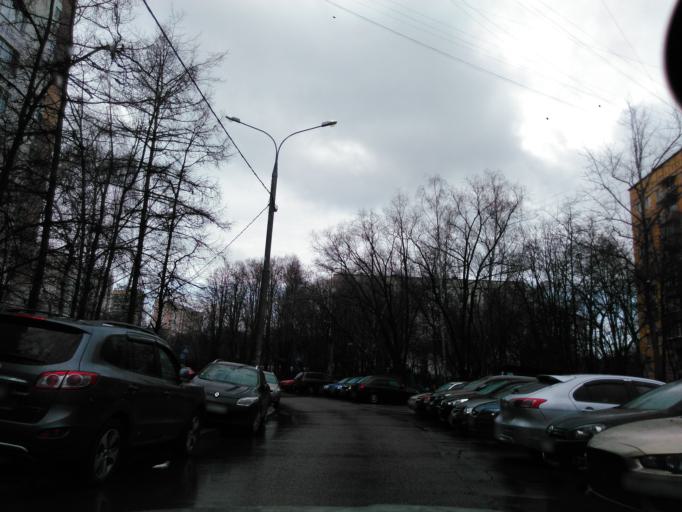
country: RU
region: Moskovskaya
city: Levoberezhnaya
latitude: 55.8670
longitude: 37.4693
